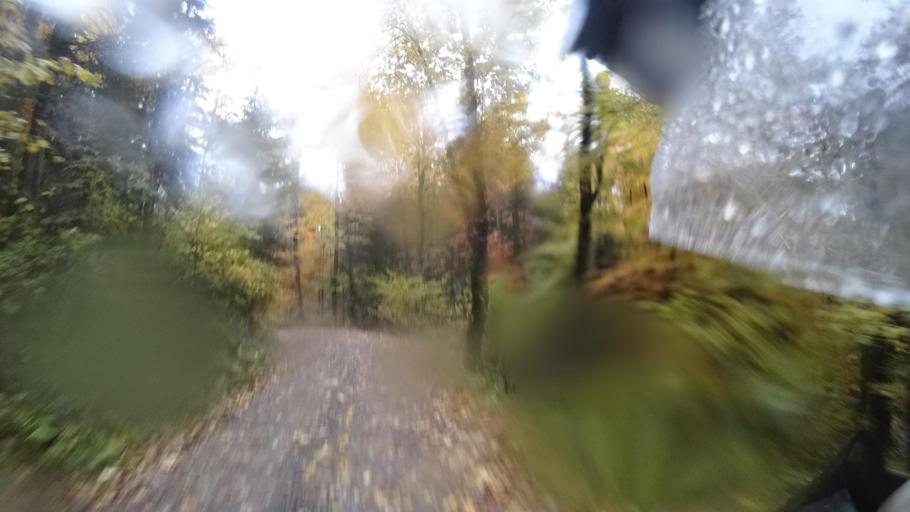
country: HR
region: Primorsko-Goranska
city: Vrbovsko
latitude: 45.3119
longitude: 15.0747
